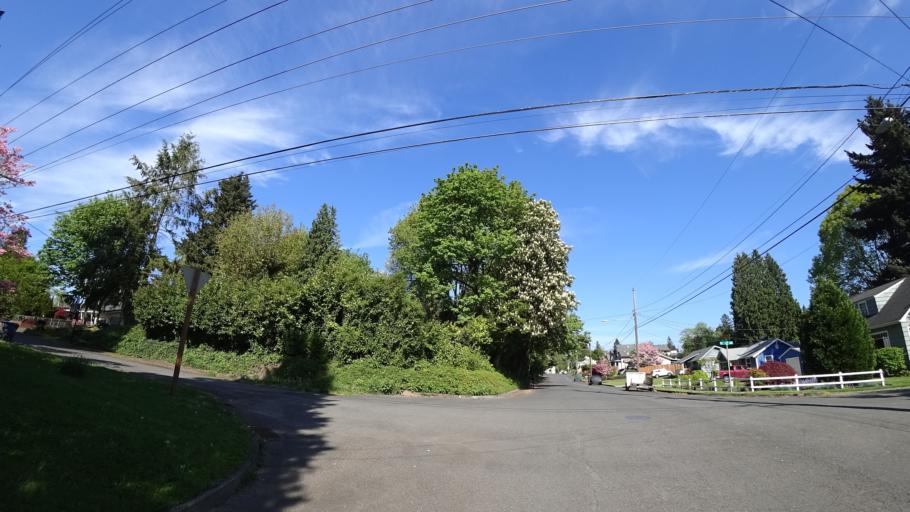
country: US
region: Oregon
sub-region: Clackamas County
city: Milwaukie
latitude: 45.4576
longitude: -122.6329
